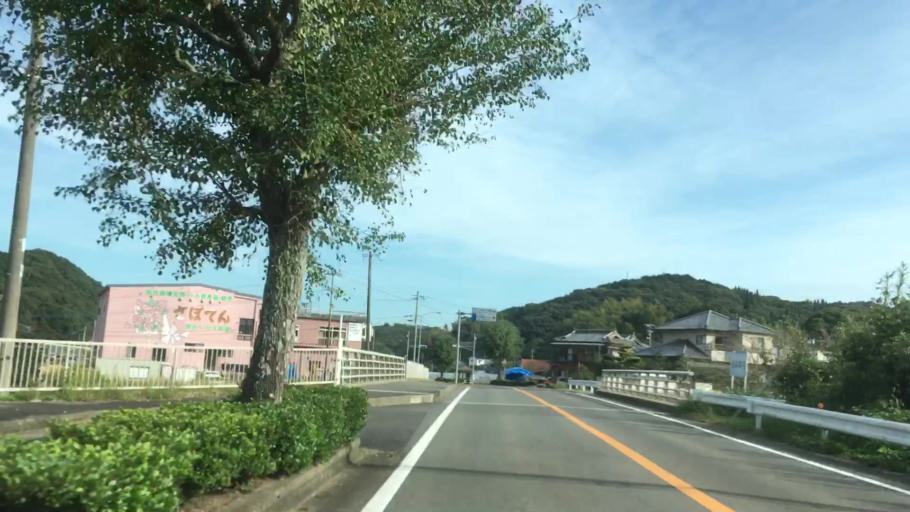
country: JP
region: Nagasaki
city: Sasebo
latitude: 32.9576
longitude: 129.6439
